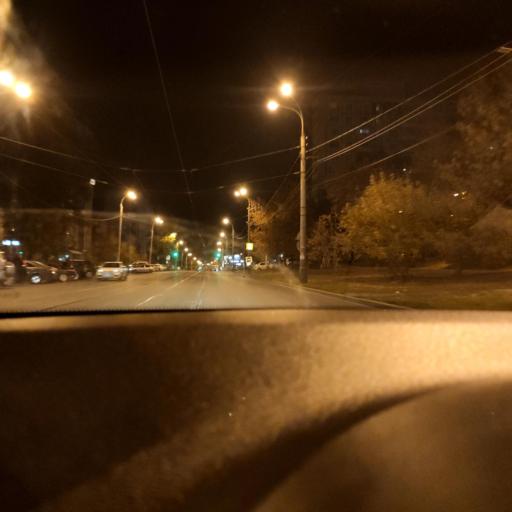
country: RU
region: Samara
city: Samara
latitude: 53.1946
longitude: 50.1489
